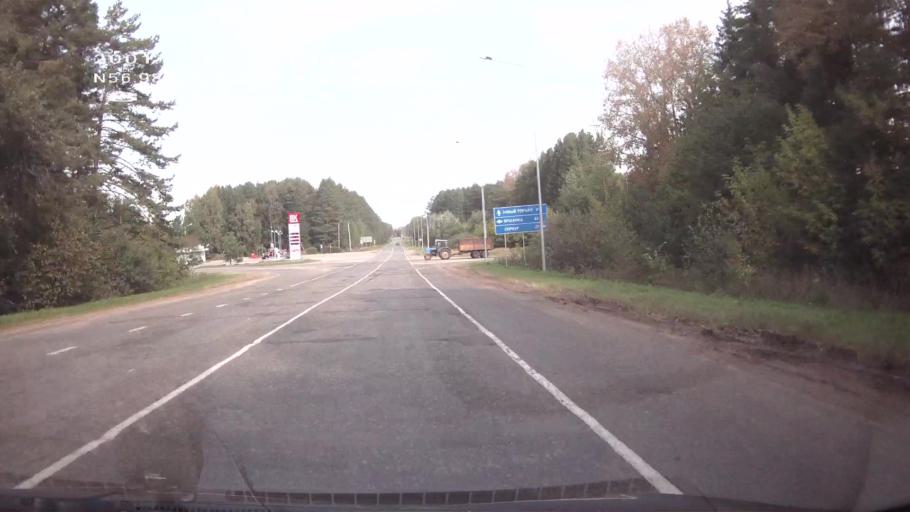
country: RU
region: Mariy-El
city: Kuzhener
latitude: 56.9843
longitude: 48.7445
